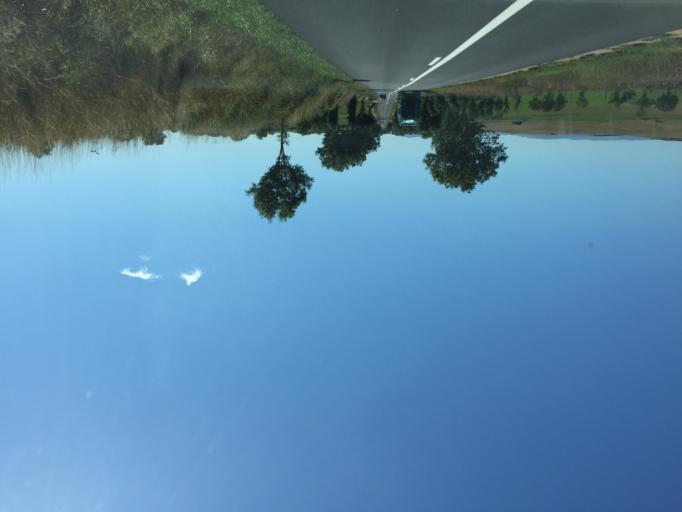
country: FR
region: Midi-Pyrenees
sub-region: Departement de l'Aveyron
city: Creissels
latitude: 44.0159
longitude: 3.0700
